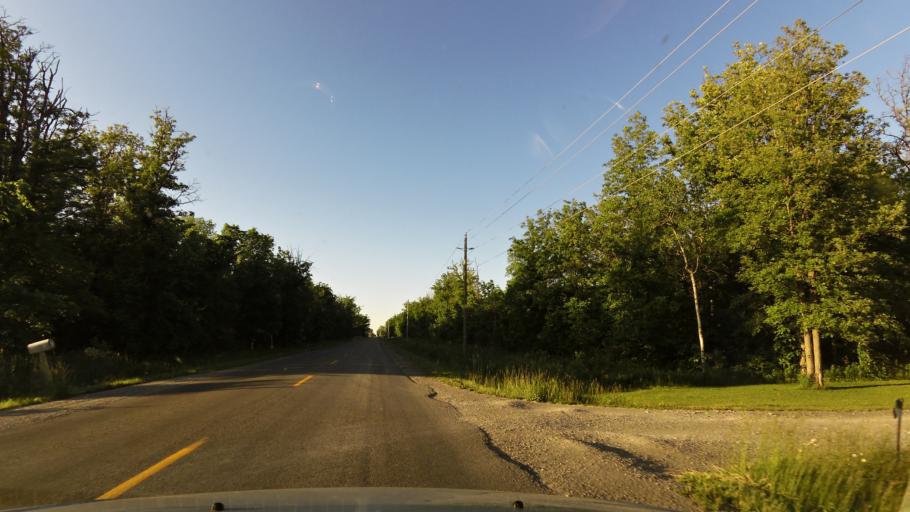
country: CA
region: Ontario
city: Ancaster
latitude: 43.0401
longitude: -80.0695
